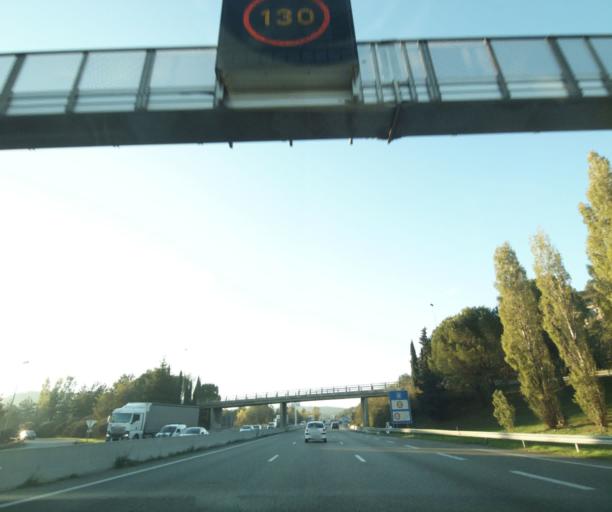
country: FR
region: Provence-Alpes-Cote d'Azur
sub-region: Departement des Bouches-du-Rhone
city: Chateauneuf-le-Rouge
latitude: 43.4844
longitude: 5.5366
